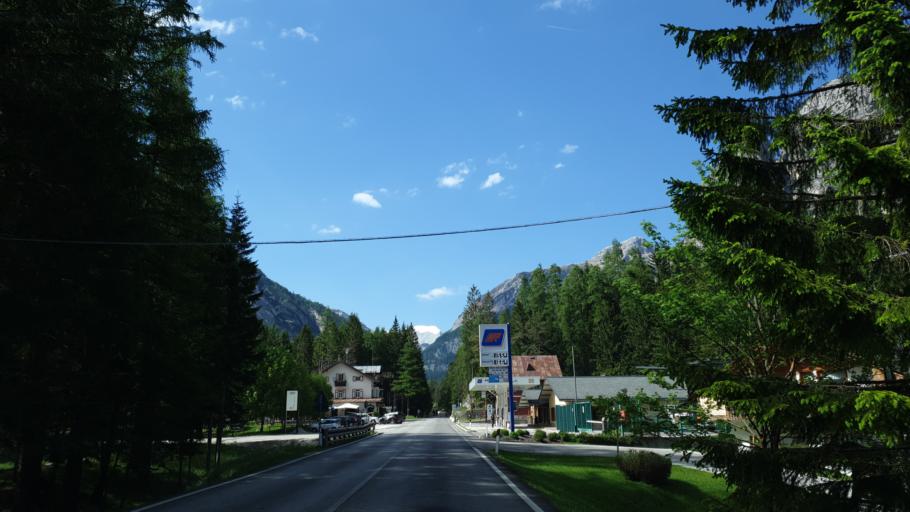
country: IT
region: Veneto
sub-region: Provincia di Belluno
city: Cortina d'Ampezzo
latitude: 46.5749
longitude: 12.1166
